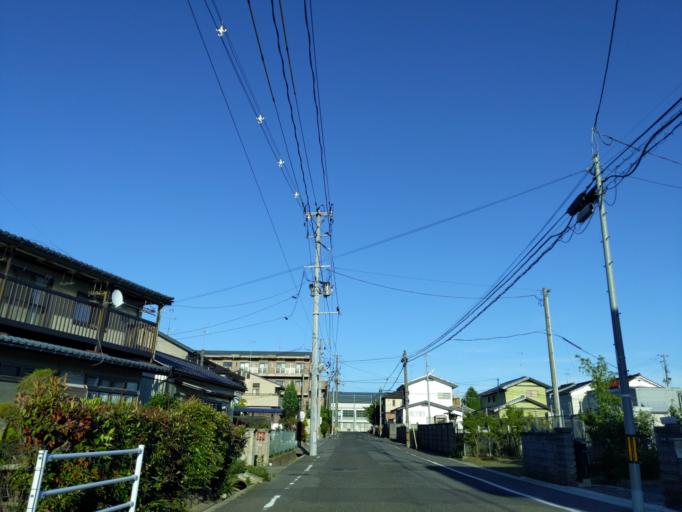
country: JP
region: Fukushima
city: Koriyama
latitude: 37.3926
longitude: 140.4051
